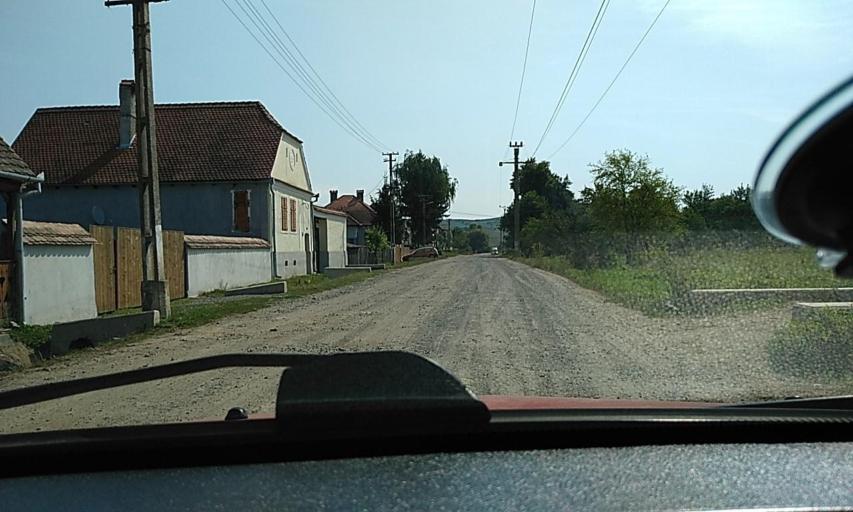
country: RO
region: Brasov
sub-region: Oras Rupea
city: Fiser
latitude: 46.0566
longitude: 25.0976
